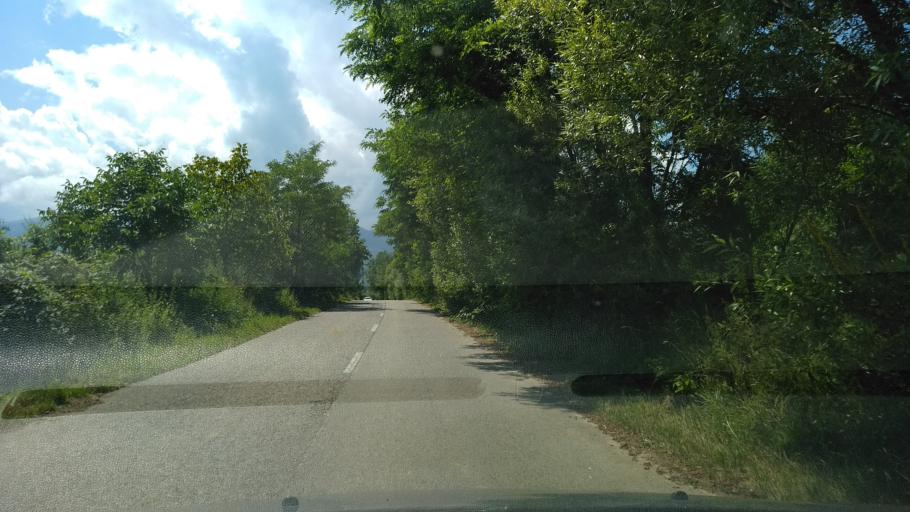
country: RO
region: Hunedoara
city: Salasu de Sus
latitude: 45.5047
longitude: 22.9504
